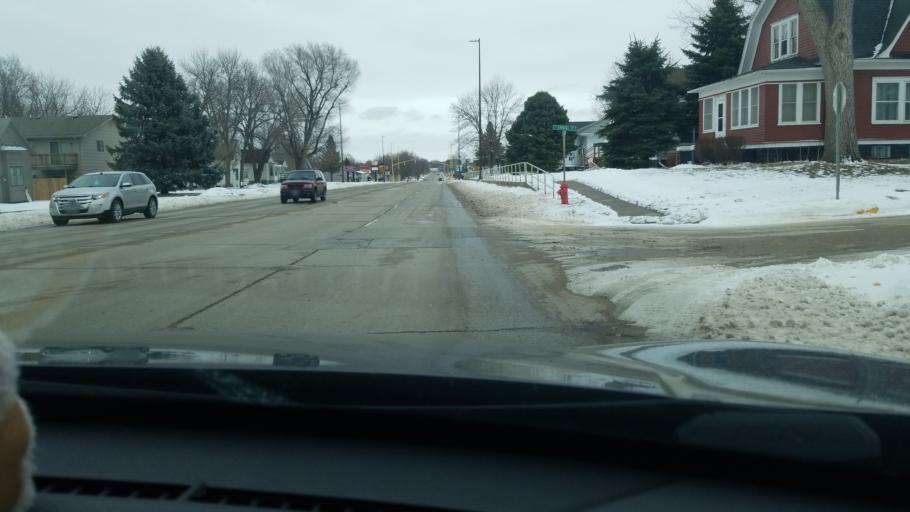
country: US
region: Iowa
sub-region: Lyon County
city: Rock Rapids
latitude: 43.4319
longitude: -96.1785
